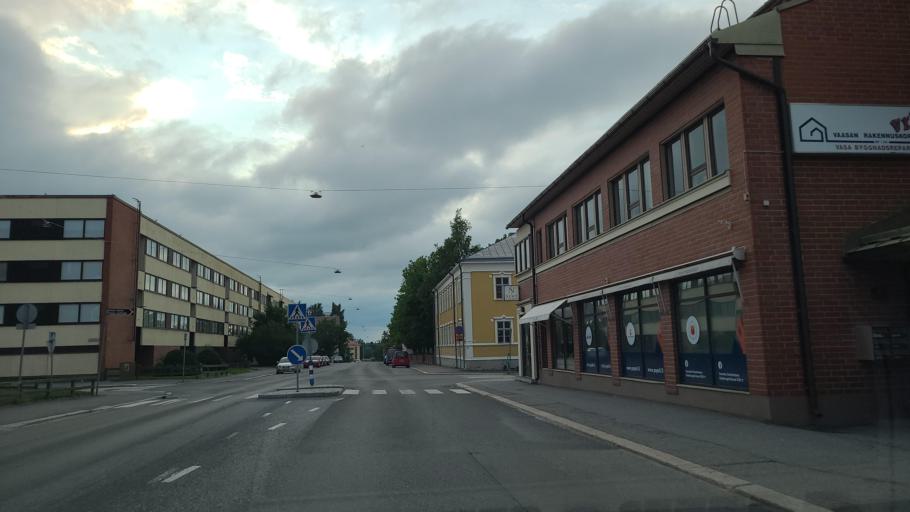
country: FI
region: Ostrobothnia
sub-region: Vaasa
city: Vaasa
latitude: 63.1020
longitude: 21.6202
